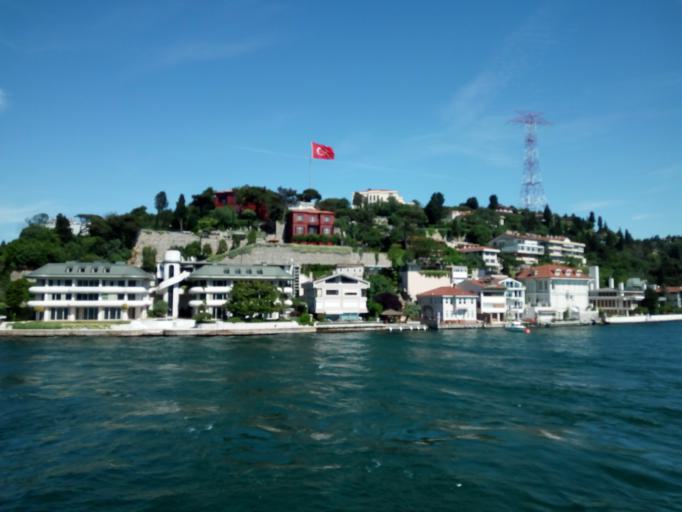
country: TR
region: Istanbul
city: UEskuedar
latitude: 41.0734
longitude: 29.0540
